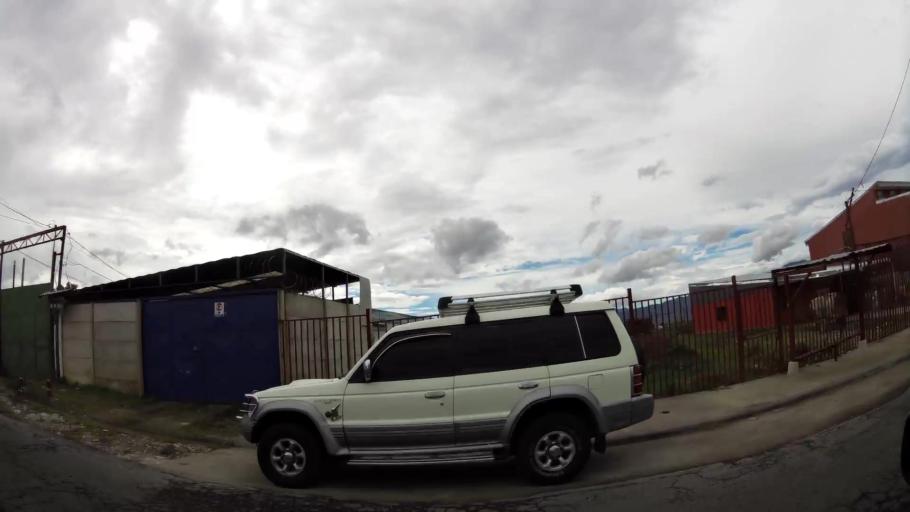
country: CR
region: San Jose
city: Purral
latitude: 9.9616
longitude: -84.0277
